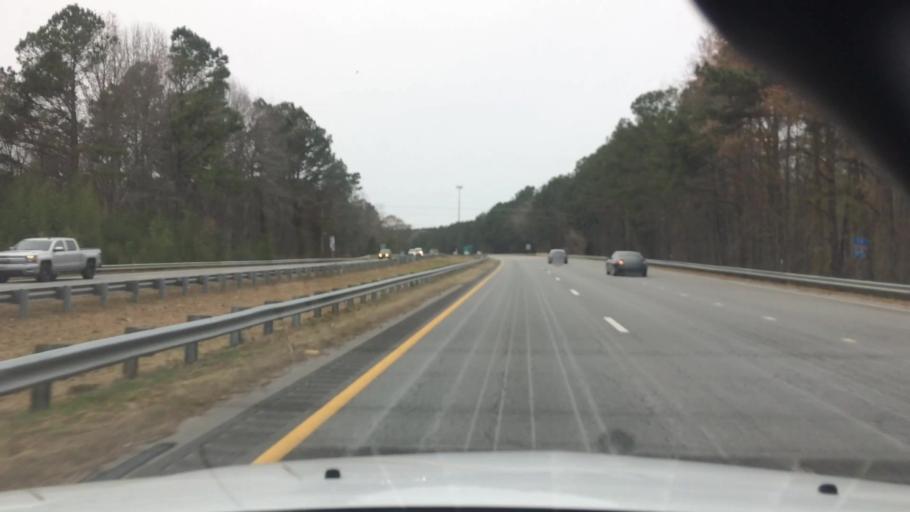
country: US
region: North Carolina
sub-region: Nash County
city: Rocky Mount
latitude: 35.9684
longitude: -77.8233
